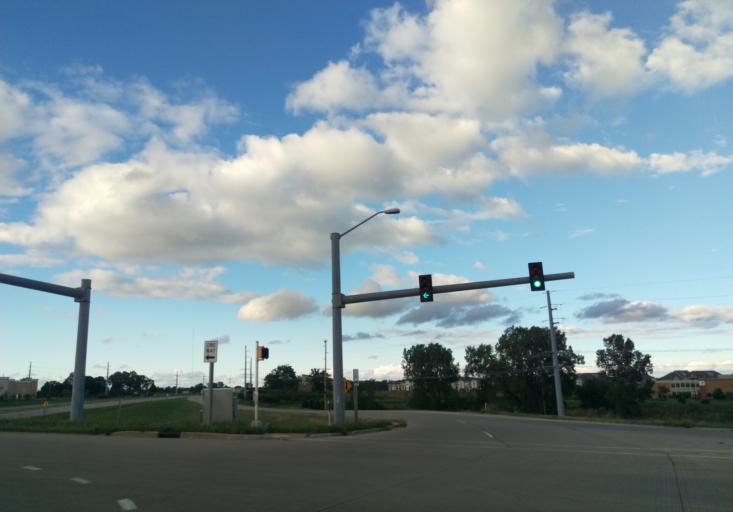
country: US
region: Wisconsin
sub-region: Dane County
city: Sun Prairie
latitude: 43.1606
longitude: -89.2670
